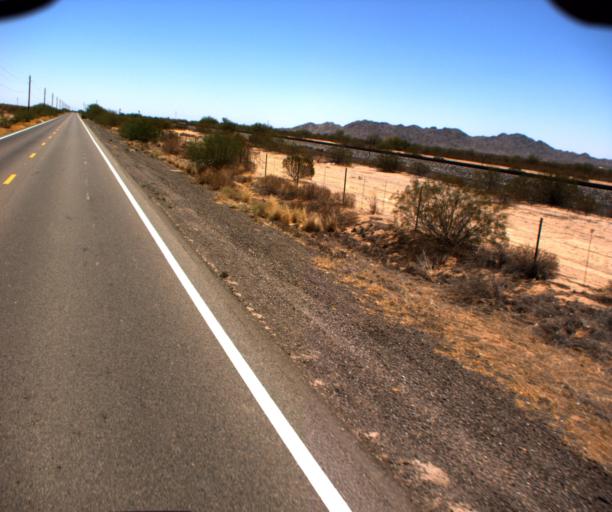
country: US
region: Arizona
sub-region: Pinal County
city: Maricopa
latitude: 33.0658
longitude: -112.2307
